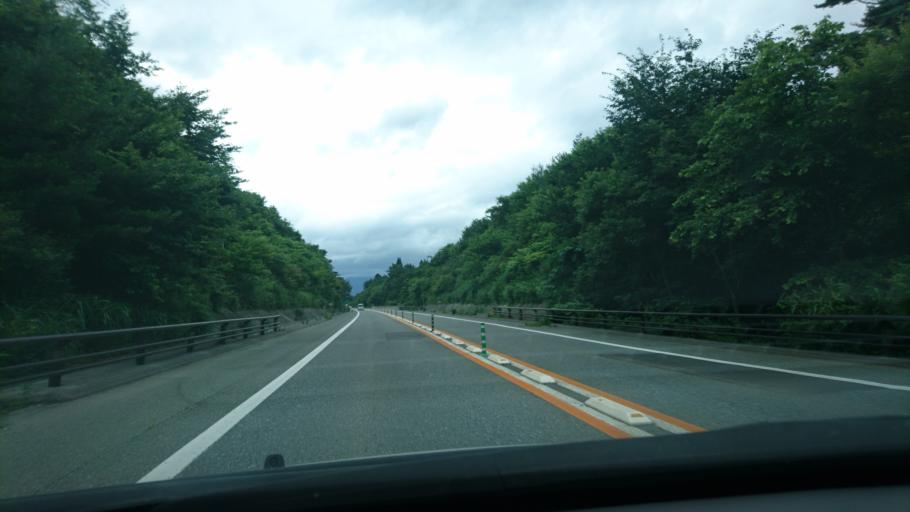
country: JP
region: Iwate
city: Ofunato
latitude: 39.0471
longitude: 141.7153
